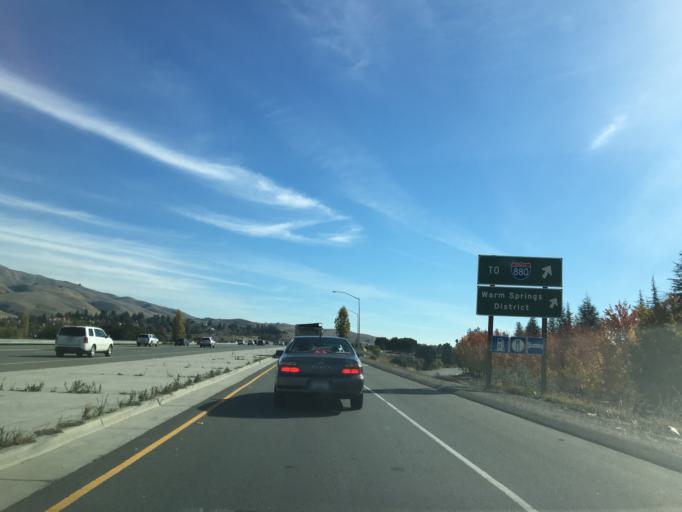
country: US
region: California
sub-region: Santa Clara County
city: Milpitas
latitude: 37.4987
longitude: -121.9272
